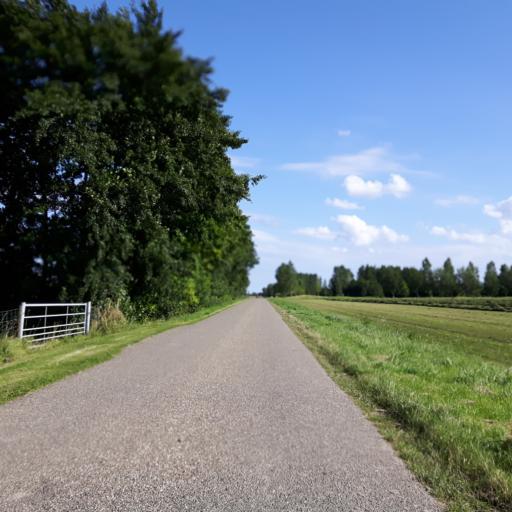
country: NL
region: Zeeland
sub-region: Gemeente Goes
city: Goes
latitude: 51.5286
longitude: 3.9174
